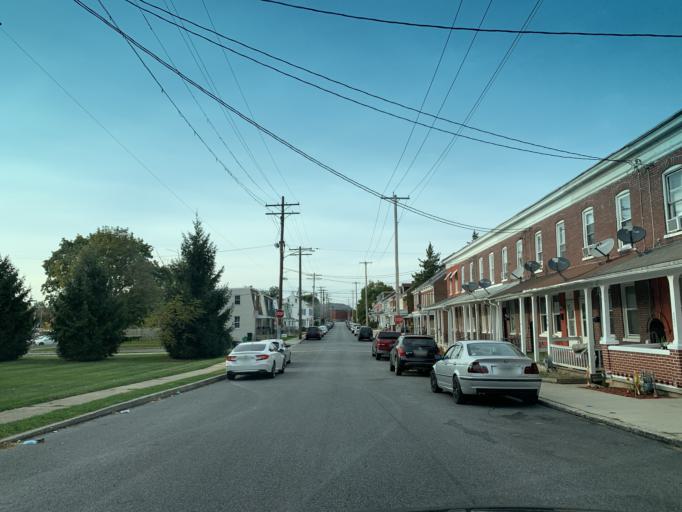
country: US
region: Pennsylvania
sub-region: York County
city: North York
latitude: 39.9684
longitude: -76.7375
